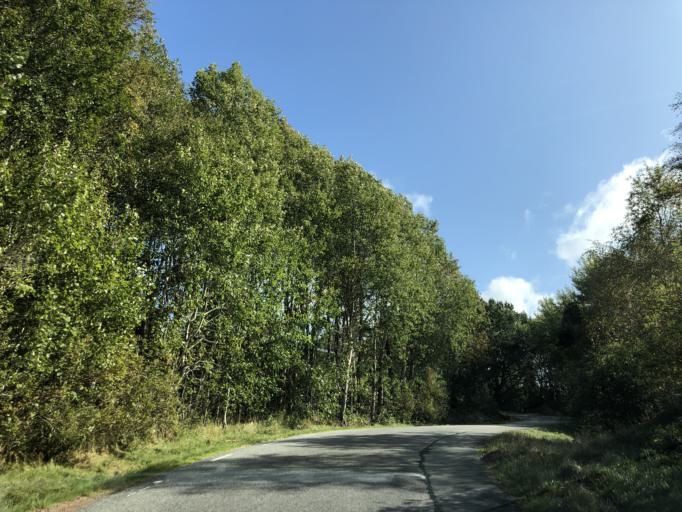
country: SE
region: Vaestra Goetaland
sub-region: Goteborg
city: Torslanda
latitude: 57.7352
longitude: 11.8405
